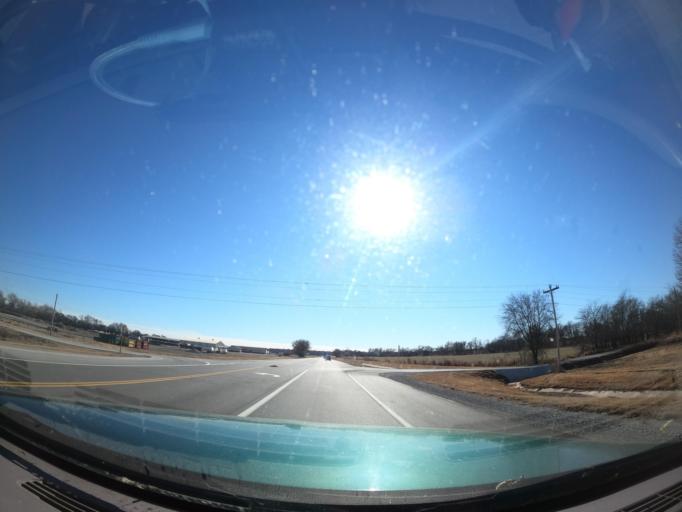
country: US
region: Oklahoma
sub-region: Wagoner County
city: Coweta
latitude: 35.8860
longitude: -95.6594
